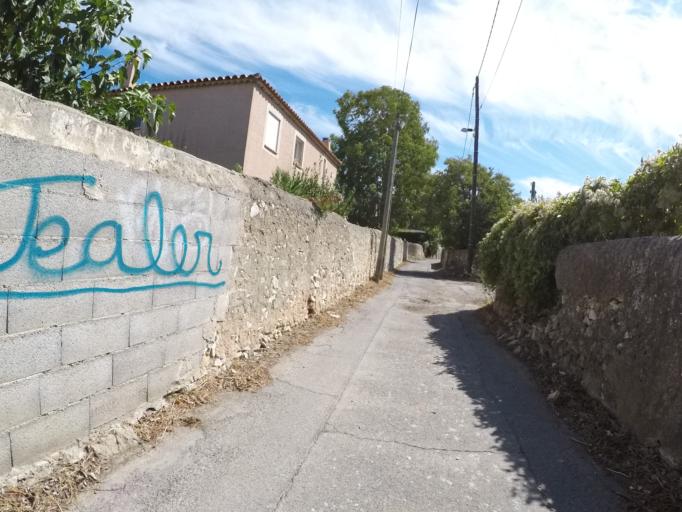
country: FR
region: Provence-Alpes-Cote d'Azur
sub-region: Departement des Bouches-du-Rhone
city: Marseille 09
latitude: 43.2377
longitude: 5.4035
